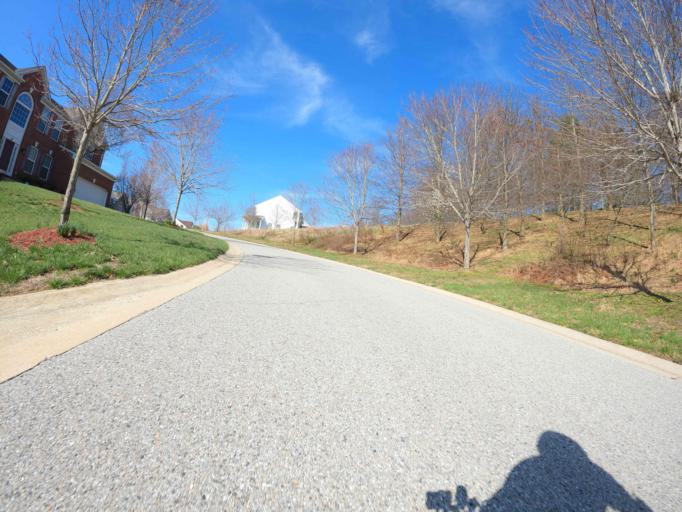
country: US
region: Maryland
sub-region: Howard County
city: Ellicott City
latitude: 39.3049
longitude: -76.8109
